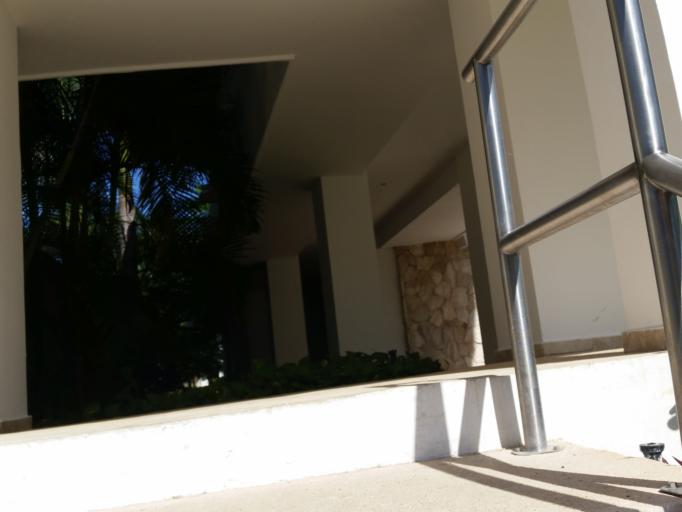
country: MX
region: Quintana Roo
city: Playa del Carmen
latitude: 20.6707
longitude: -87.0339
